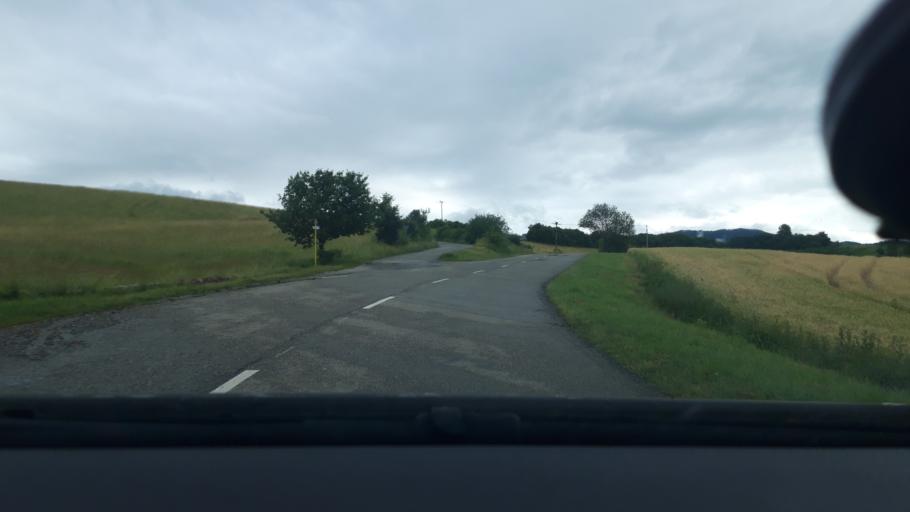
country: SK
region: Zilinsky
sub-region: Okres Martin
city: Martin
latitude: 49.0150
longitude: 18.9961
